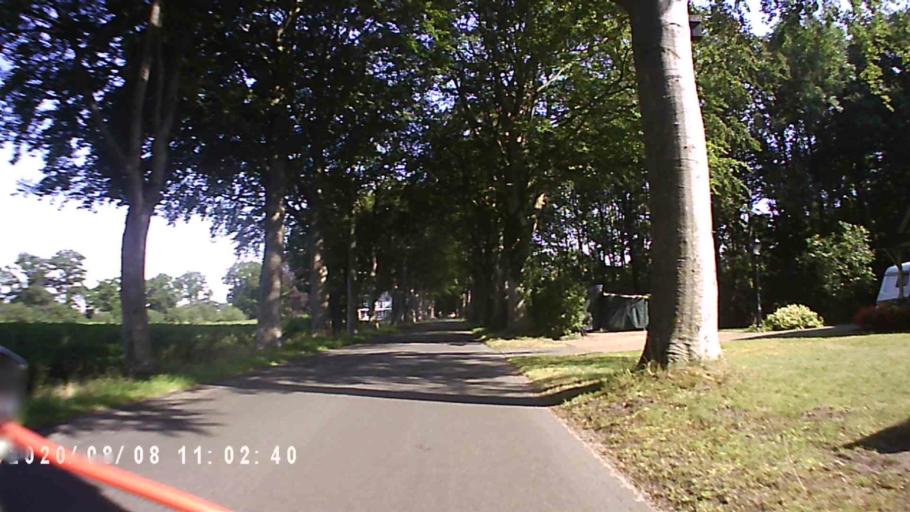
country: NL
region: Groningen
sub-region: Gemeente Leek
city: Leek
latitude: 53.1558
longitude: 6.3951
